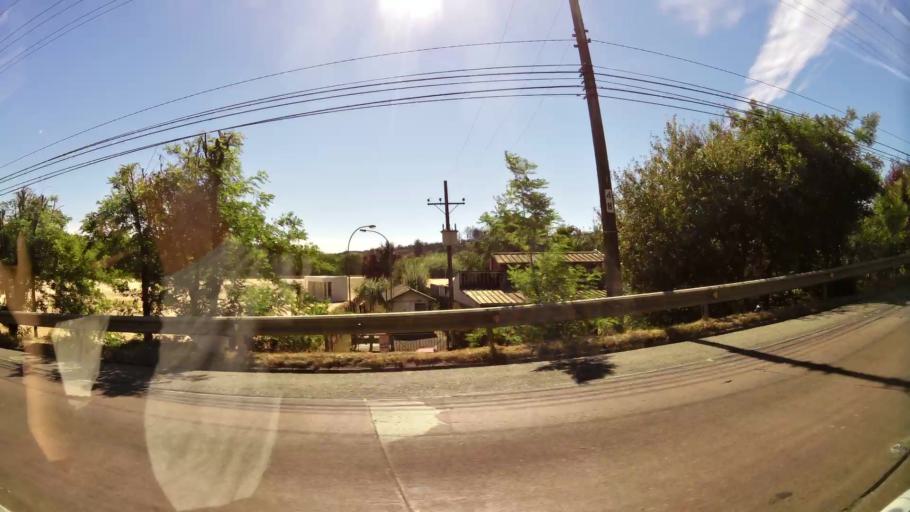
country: CL
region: Biobio
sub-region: Provincia de Concepcion
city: Penco
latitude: -36.7692
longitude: -73.0134
